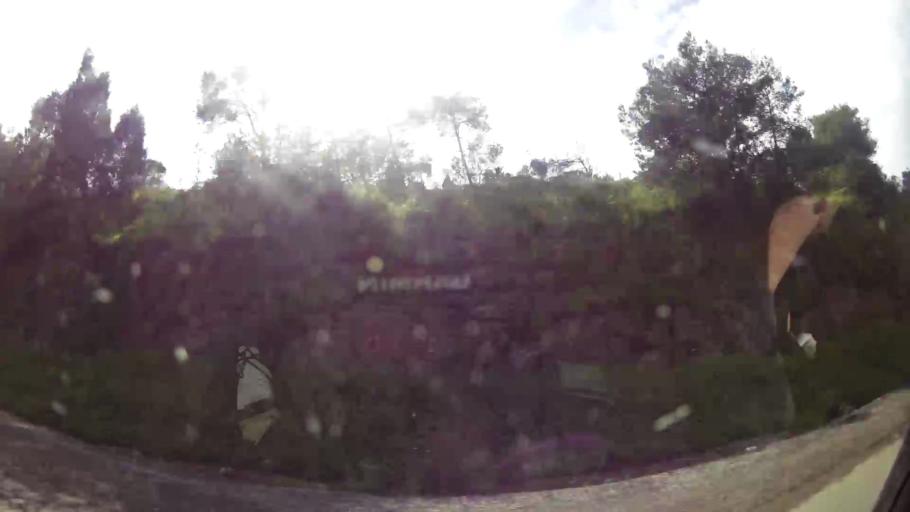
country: MA
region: Grand Casablanca
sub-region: Mohammedia
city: Mohammedia
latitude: 33.6568
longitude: -7.4002
